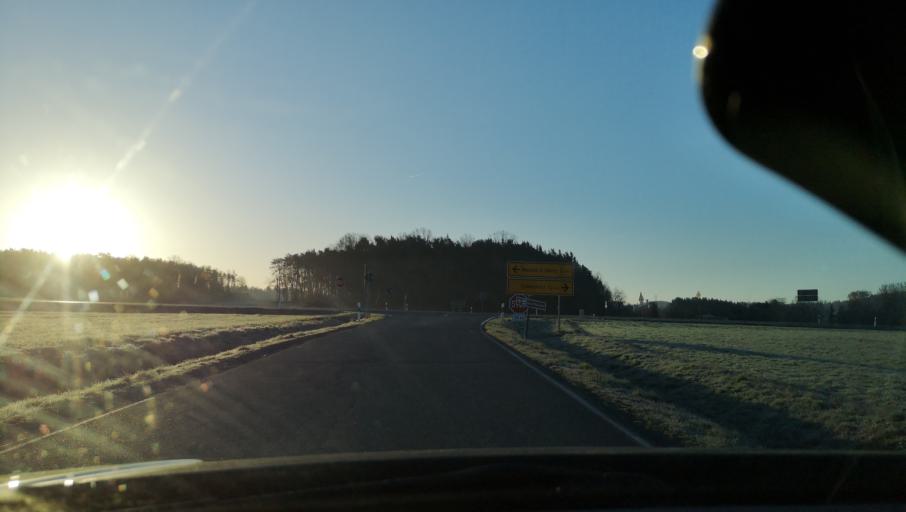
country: DE
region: Bavaria
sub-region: Upper Franconia
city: Neustadt bei Coburg
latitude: 50.3070
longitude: 11.1073
